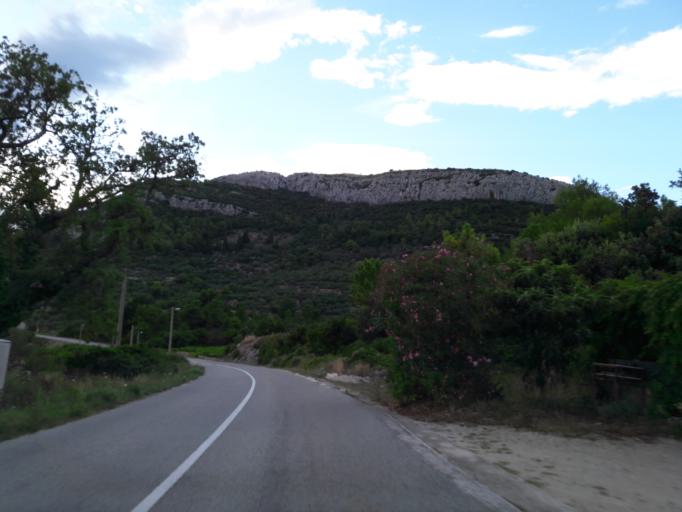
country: HR
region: Dubrovacko-Neretvanska
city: Ston
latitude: 42.8463
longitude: 17.6305
